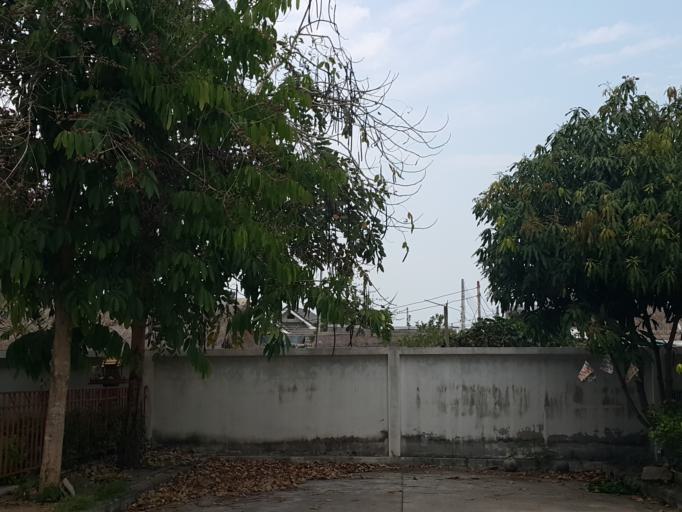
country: TH
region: Chiang Mai
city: Saraphi
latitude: 18.7708
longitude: 99.0510
